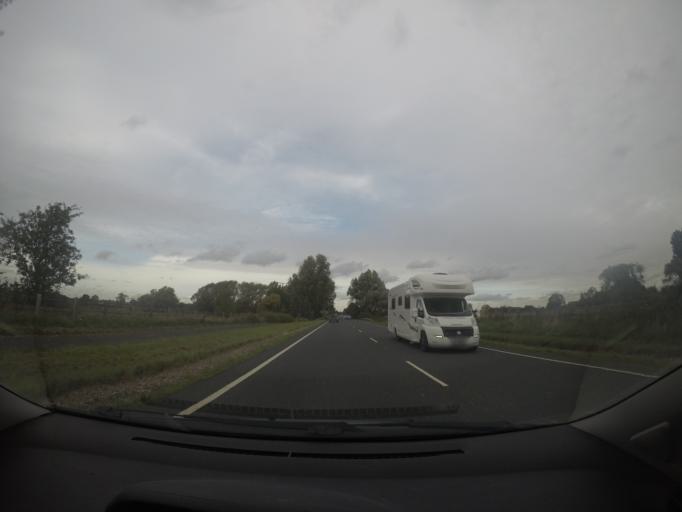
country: GB
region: England
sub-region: North Yorkshire
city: Riccall
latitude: 53.8247
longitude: -1.0486
